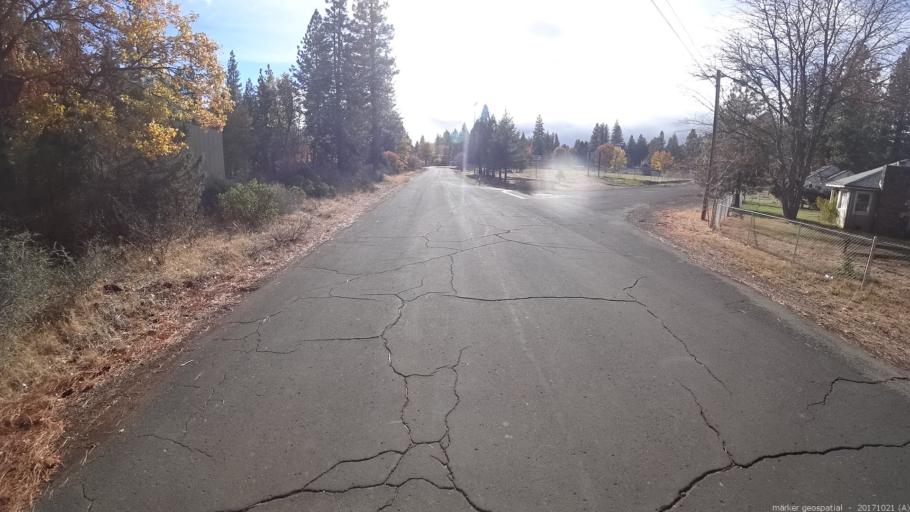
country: US
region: California
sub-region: Shasta County
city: Burney
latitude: 40.8773
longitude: -121.6630
